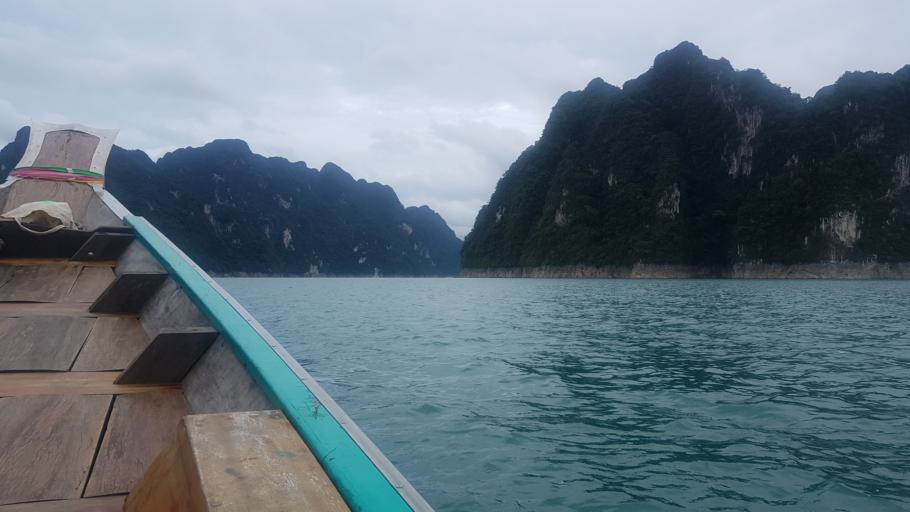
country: TH
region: Surat Thani
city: Phanom
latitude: 9.0259
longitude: 98.7217
